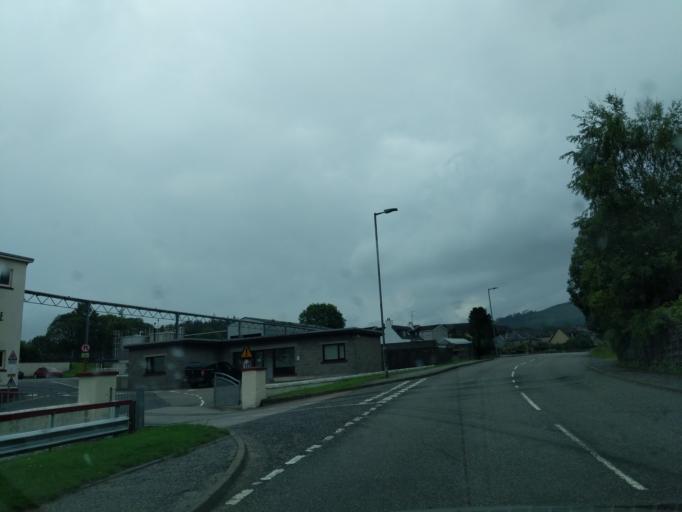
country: GB
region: Scotland
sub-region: Moray
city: Rothes
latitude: 57.4883
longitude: -3.1855
